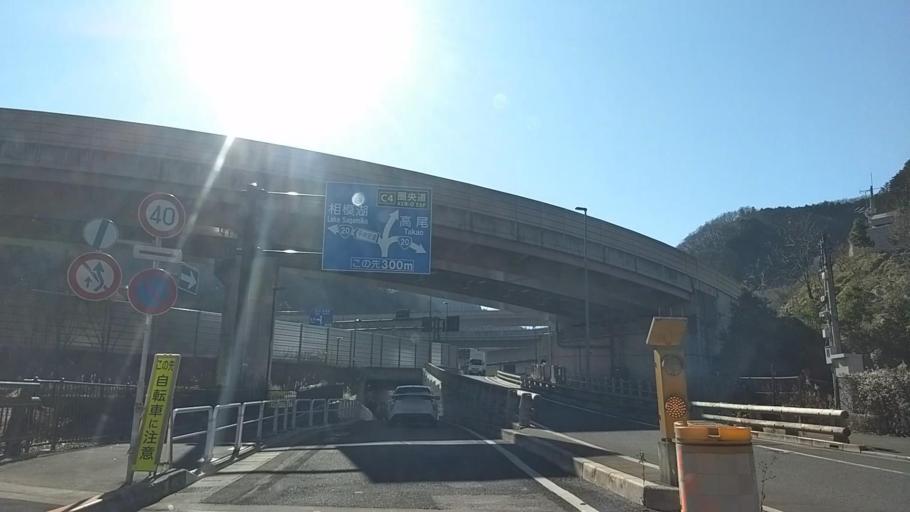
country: JP
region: Tokyo
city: Hachioji
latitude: 35.6261
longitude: 139.2638
